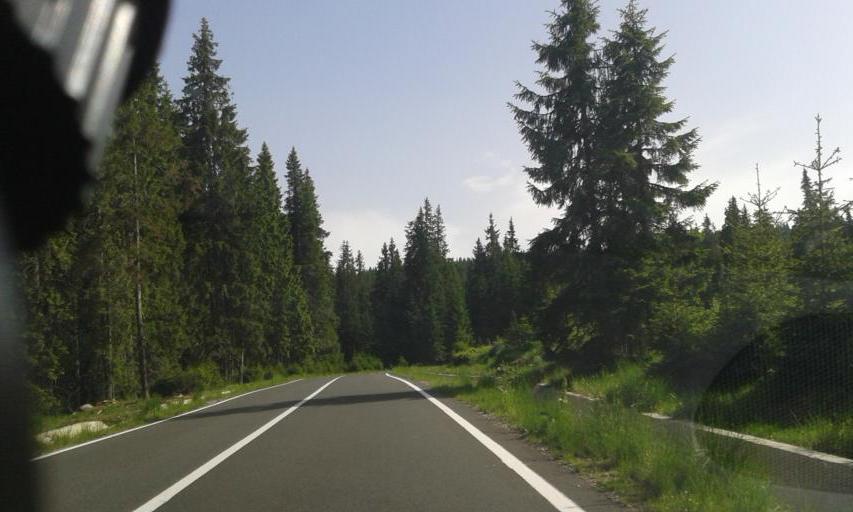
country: RO
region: Hunedoara
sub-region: Oras Petrila
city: Petrila
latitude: 45.4851
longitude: 23.6398
